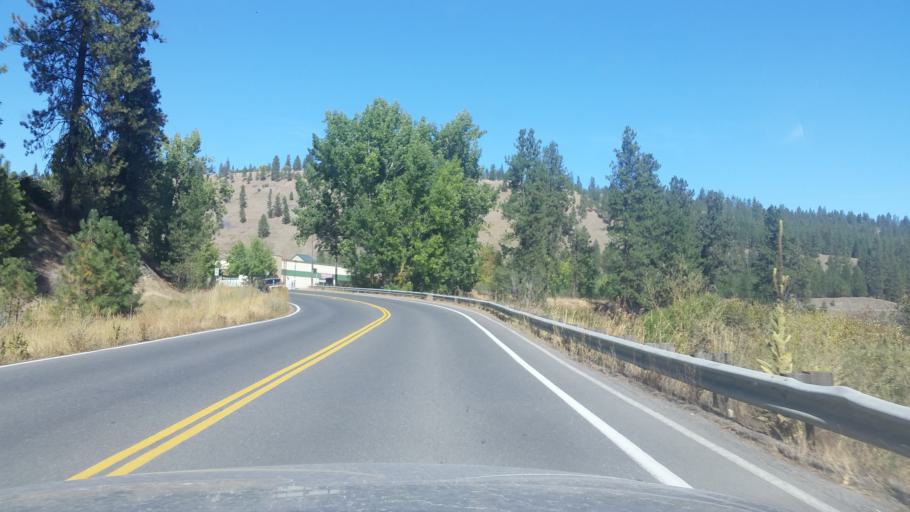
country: US
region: Washington
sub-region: Spokane County
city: Spokane
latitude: 47.6130
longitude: -117.4304
